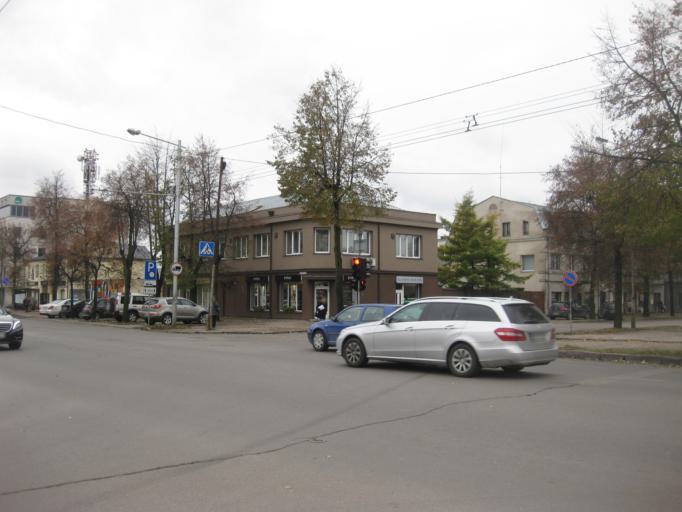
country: LT
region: Kauno apskritis
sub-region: Kaunas
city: Kaunas
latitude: 54.9058
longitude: 23.9207
